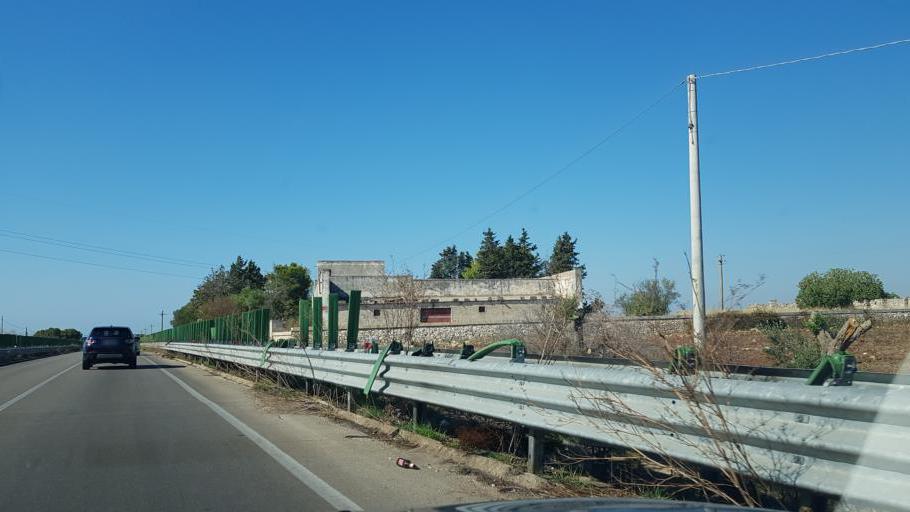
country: IT
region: Apulia
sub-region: Provincia di Lecce
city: Porto Cesareo
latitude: 40.2727
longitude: 17.9287
